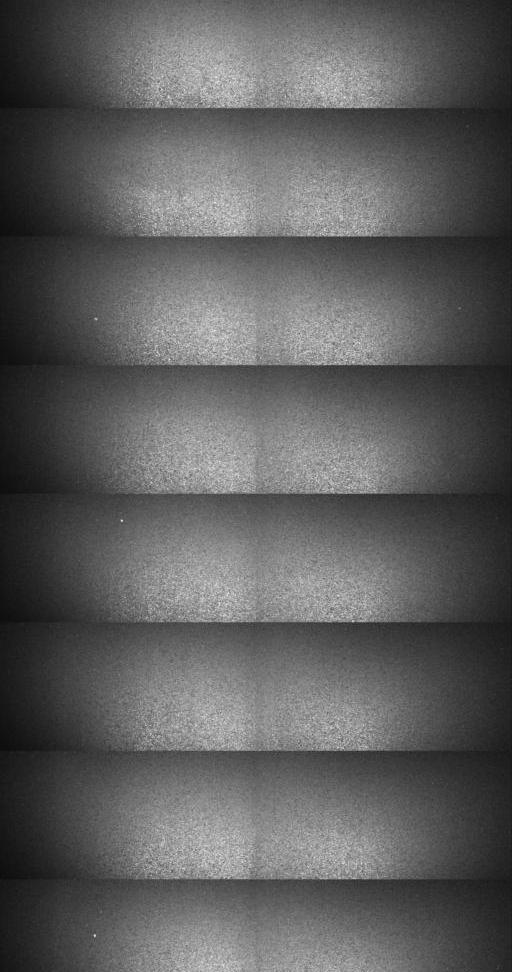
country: US
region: Vermont
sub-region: Franklin County
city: Richford
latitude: 44.9757
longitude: -72.5202
